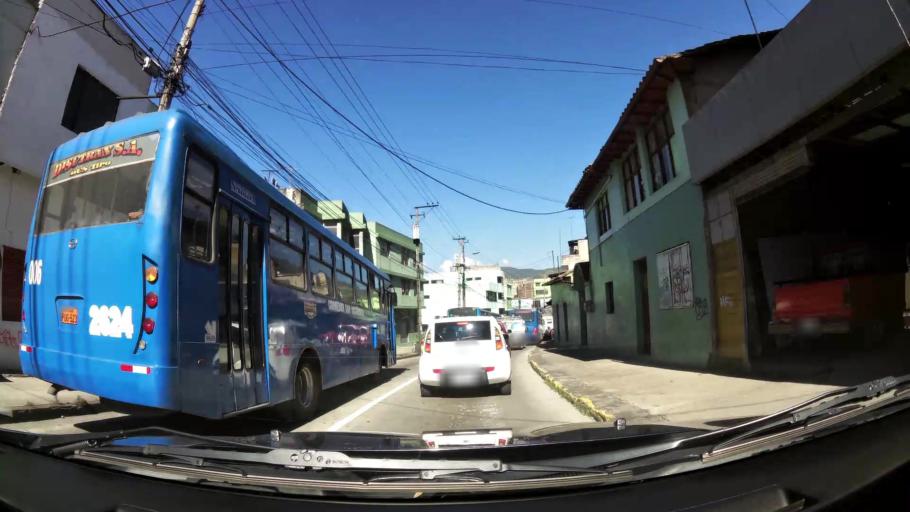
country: EC
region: Pichincha
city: Quito
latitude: -0.2356
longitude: -78.5260
